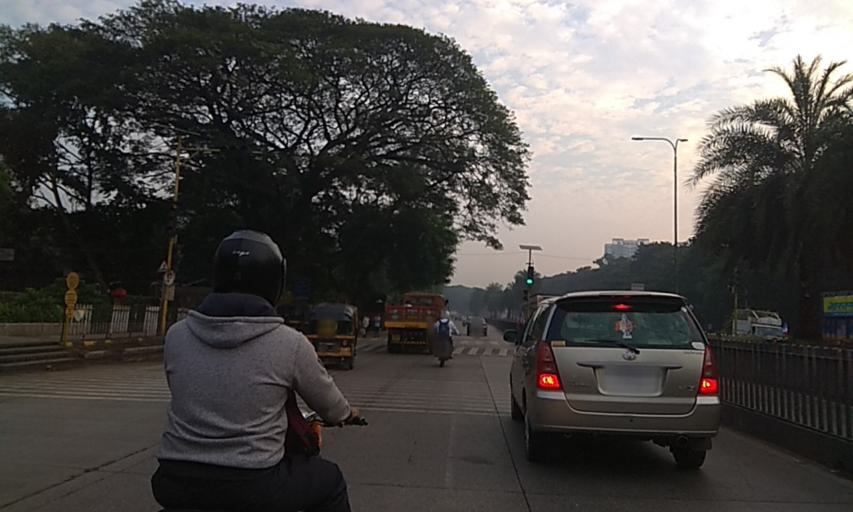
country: IN
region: Maharashtra
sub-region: Pune Division
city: Khadki
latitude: 18.5479
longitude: 73.8917
